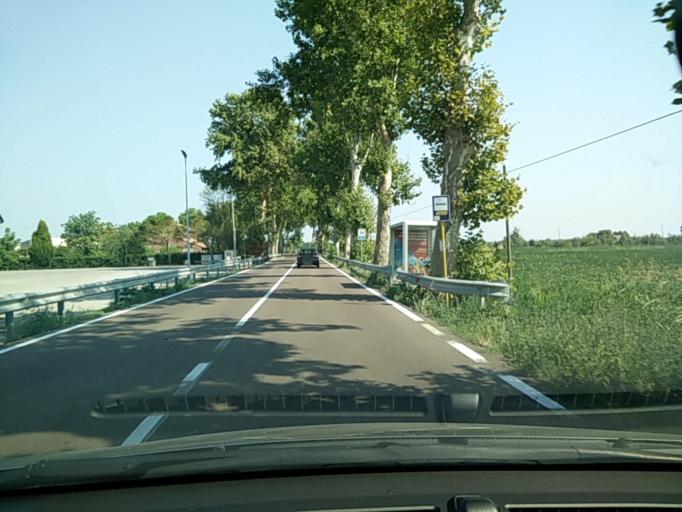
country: IT
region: Veneto
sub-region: Provincia di Venezia
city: San Giorgio di Livenza
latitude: 45.6482
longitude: 12.7758
